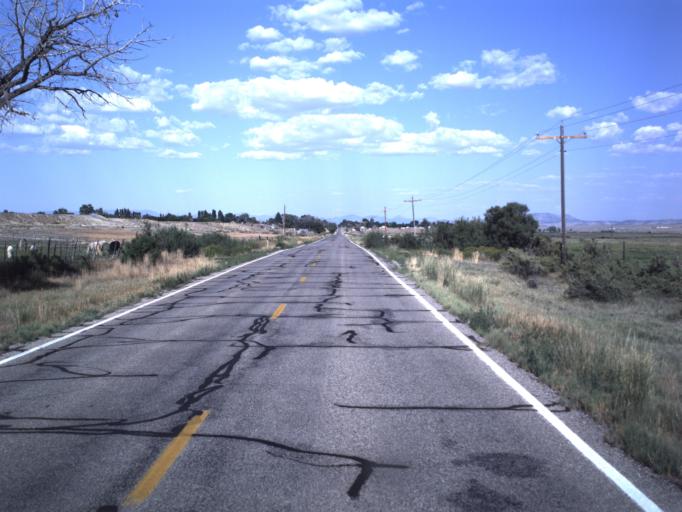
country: US
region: Utah
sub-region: Emery County
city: Huntington
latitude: 39.3465
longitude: -110.8801
